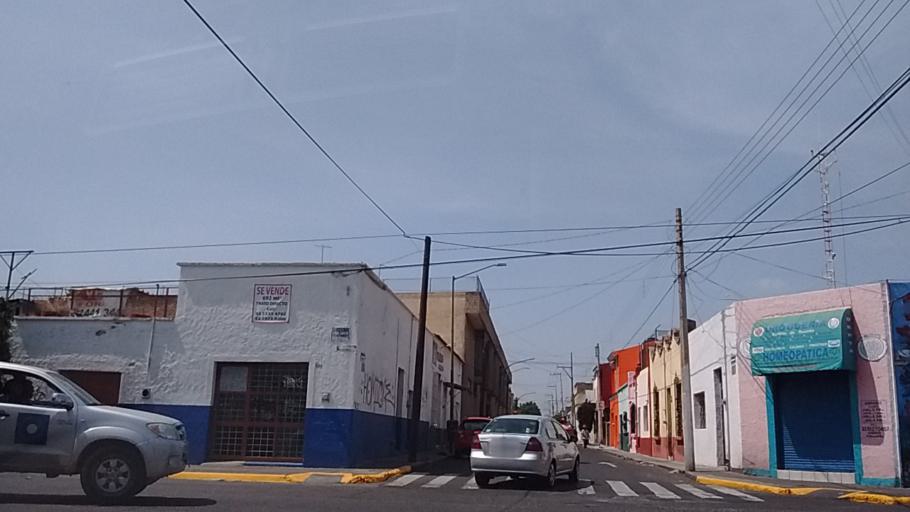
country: MX
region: Jalisco
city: Guadalajara
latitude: 20.6897
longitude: -103.3465
